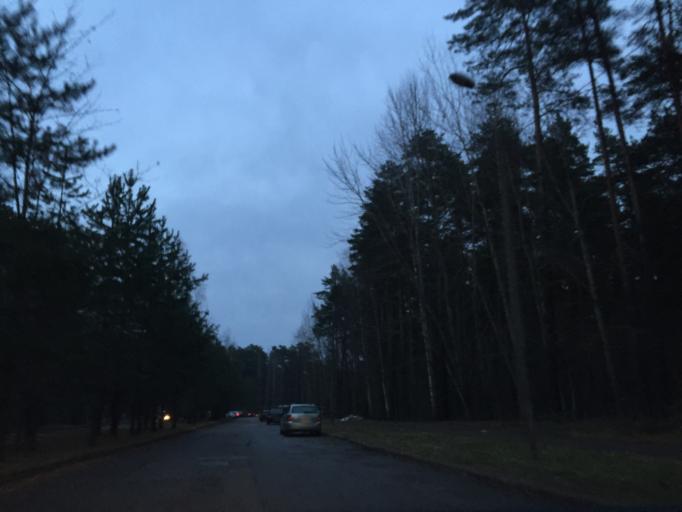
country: LV
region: Riga
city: Jaunciems
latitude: 57.0406
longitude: 24.1874
